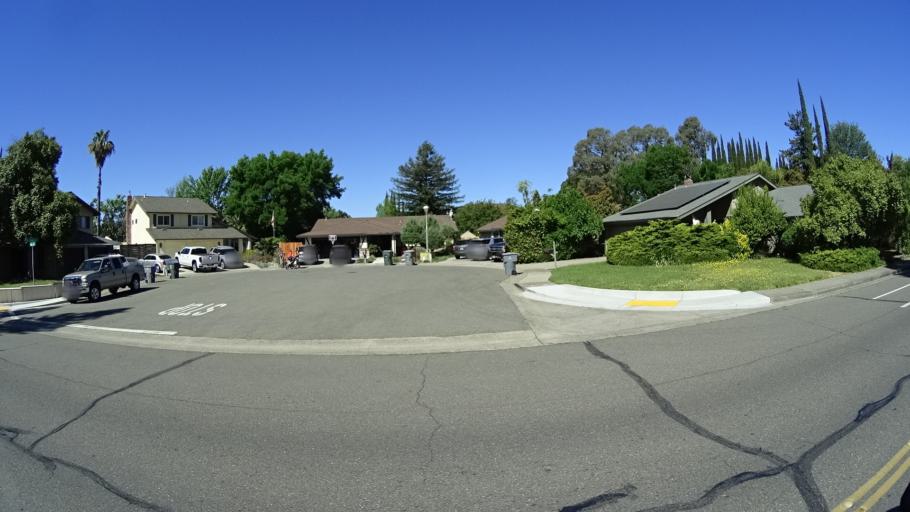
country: US
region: California
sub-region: Placer County
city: Rocklin
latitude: 38.7804
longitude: -121.2491
